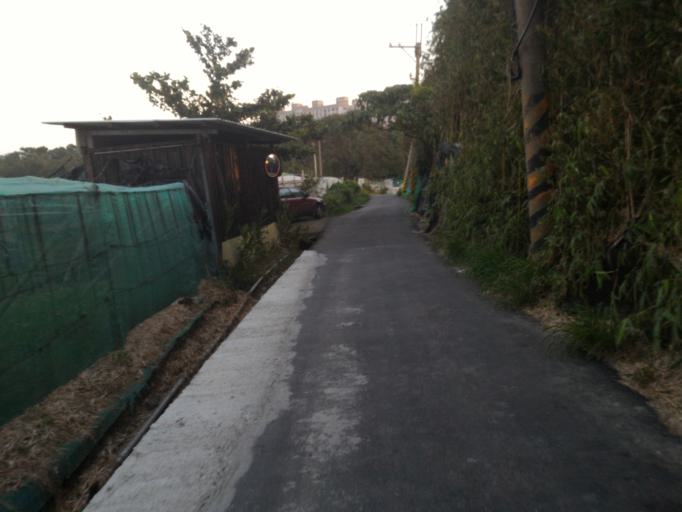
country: TW
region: Taiwan
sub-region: Taoyuan
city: Taoyuan
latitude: 24.9530
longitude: 121.3829
